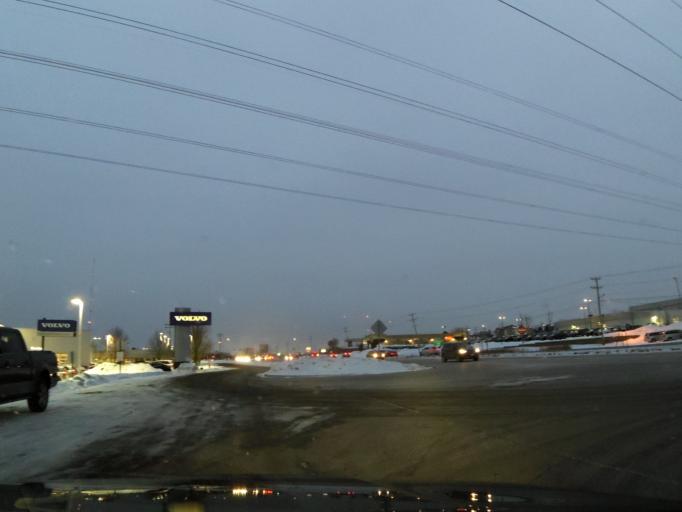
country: US
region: Minnesota
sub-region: Ramsey County
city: Vadnais Heights
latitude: 45.0344
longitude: -93.0441
